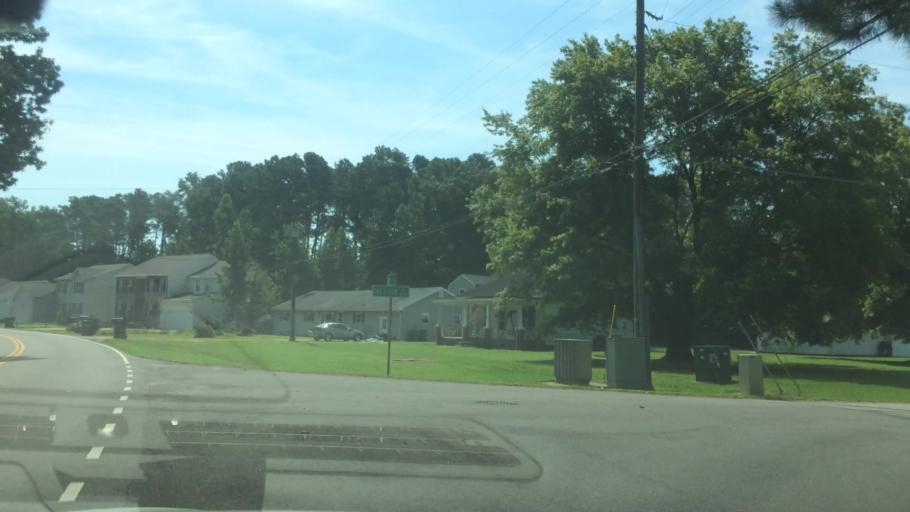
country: US
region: Virginia
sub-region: City of Poquoson
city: Poquoson
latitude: 37.1625
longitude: -76.4261
